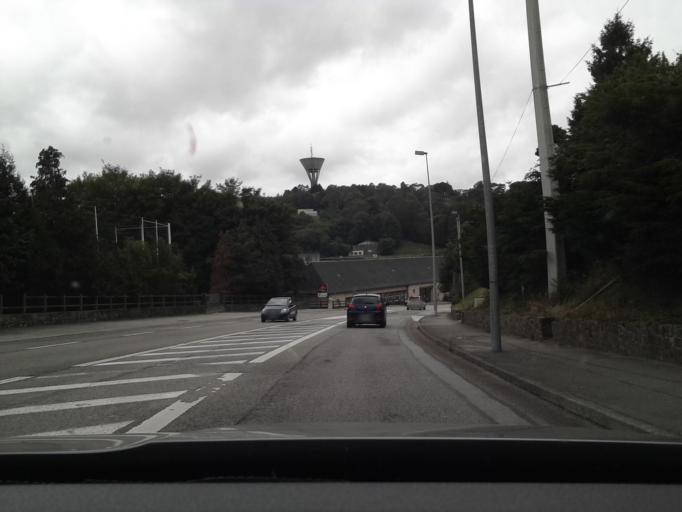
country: FR
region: Lower Normandy
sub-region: Departement de la Manche
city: Cherbourg-Octeville
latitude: 49.6235
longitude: -1.6140
